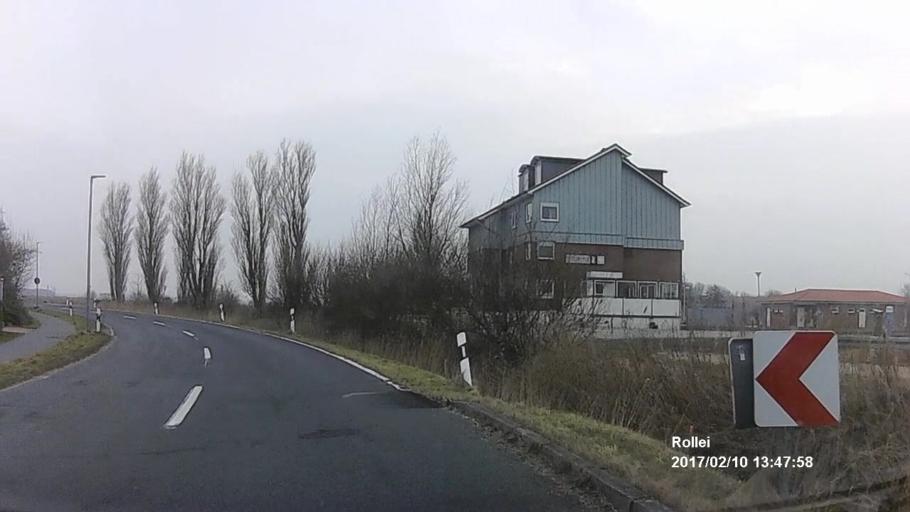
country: DE
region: Lower Saxony
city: Norddeich
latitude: 53.6028
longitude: 7.1354
